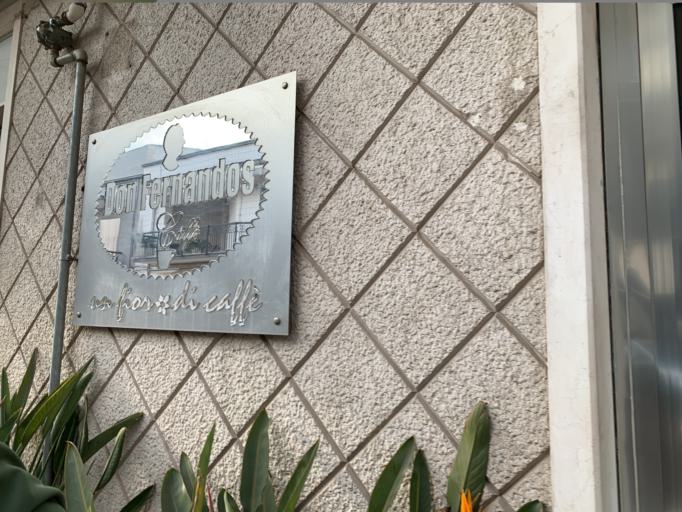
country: IT
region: Apulia
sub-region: Provincia di Barletta - Andria - Trani
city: Andria
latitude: 41.2302
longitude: 16.2869
